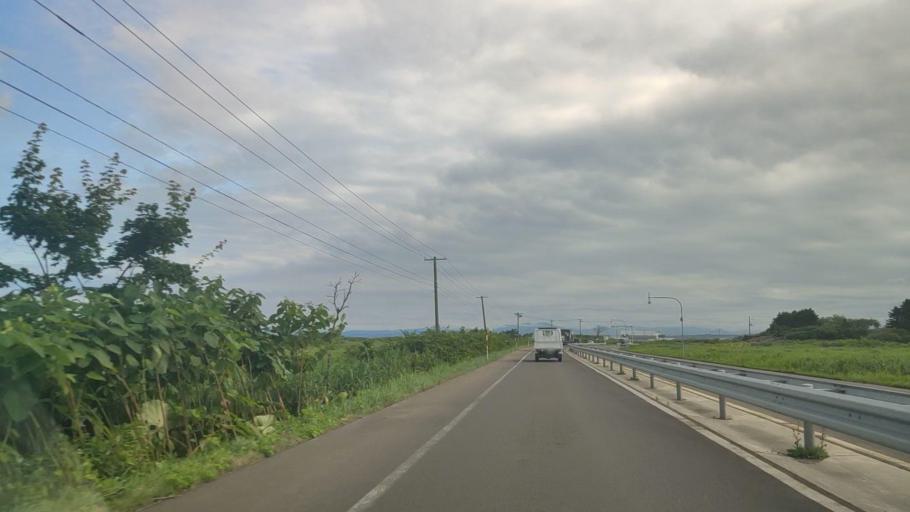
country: JP
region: Hokkaido
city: Niseko Town
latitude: 42.4507
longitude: 140.3314
